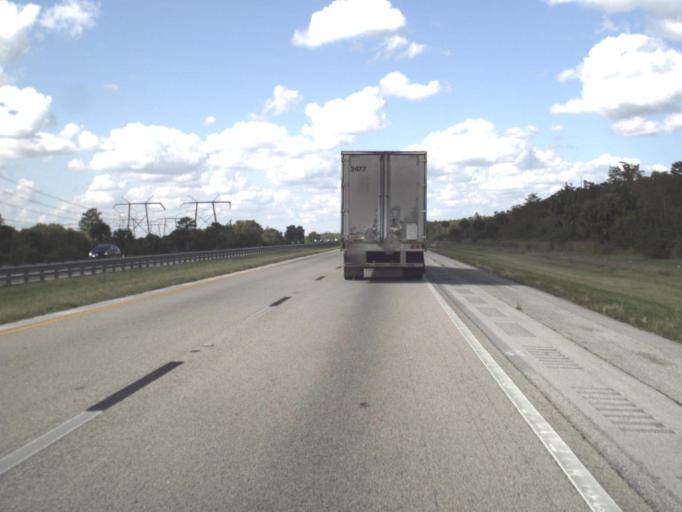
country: US
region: Florida
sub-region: Indian River County
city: West Vero Corridor
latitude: 27.5526
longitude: -80.6362
